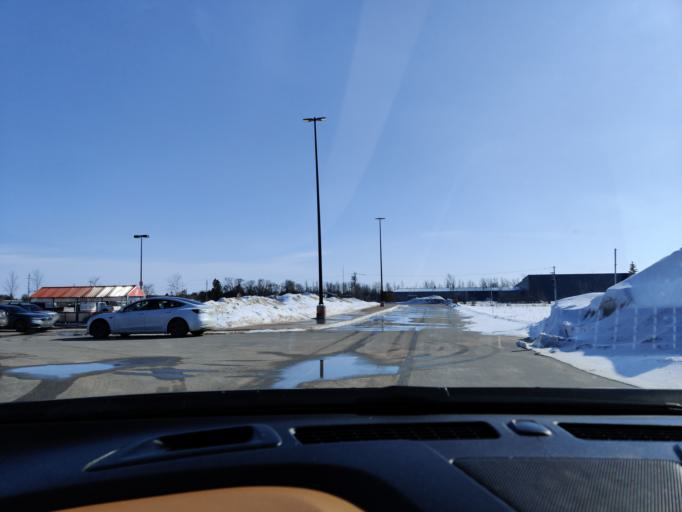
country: CA
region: Ontario
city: Collingwood
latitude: 44.4989
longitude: -80.2364
